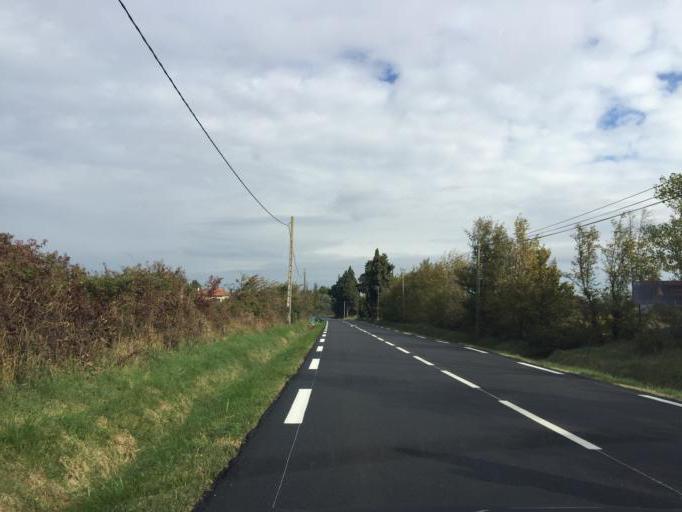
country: FR
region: Provence-Alpes-Cote d'Azur
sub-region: Departement du Vaucluse
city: Orange
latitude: 44.1642
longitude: 4.8051
